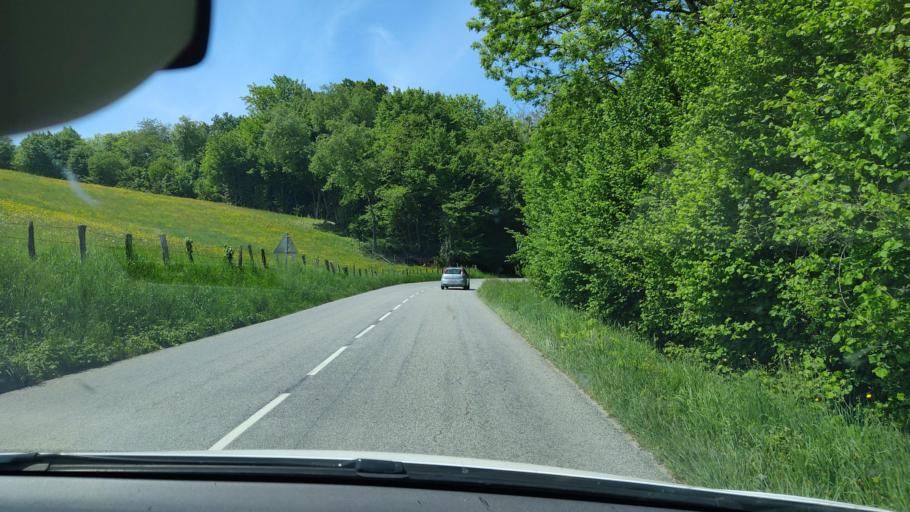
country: FR
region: Rhone-Alpes
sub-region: Departement de la Savoie
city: La Bridoire
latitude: 45.5260
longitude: 5.7332
